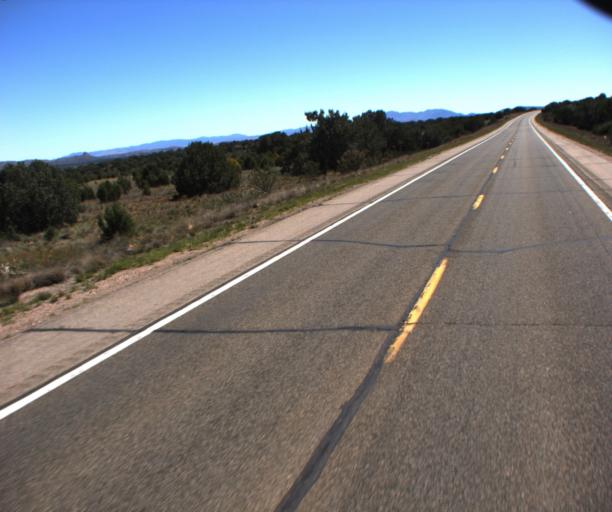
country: US
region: Arizona
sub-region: Yavapai County
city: Paulden
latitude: 34.9446
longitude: -112.4265
